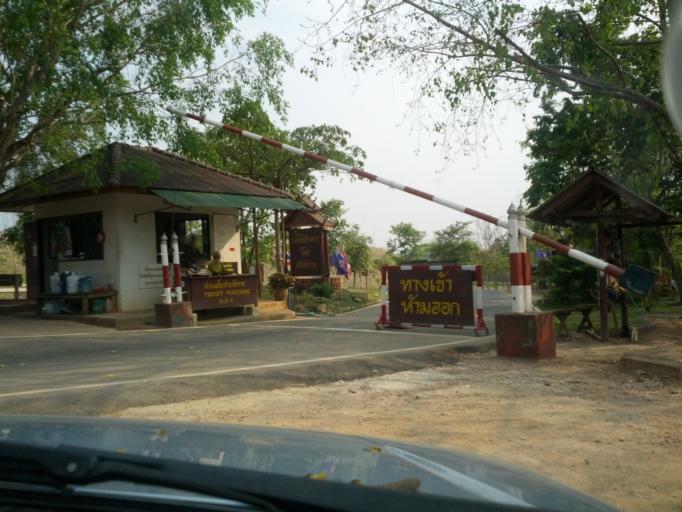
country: TH
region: Chiang Mai
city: Mae Taeng
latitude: 19.1748
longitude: 99.0310
